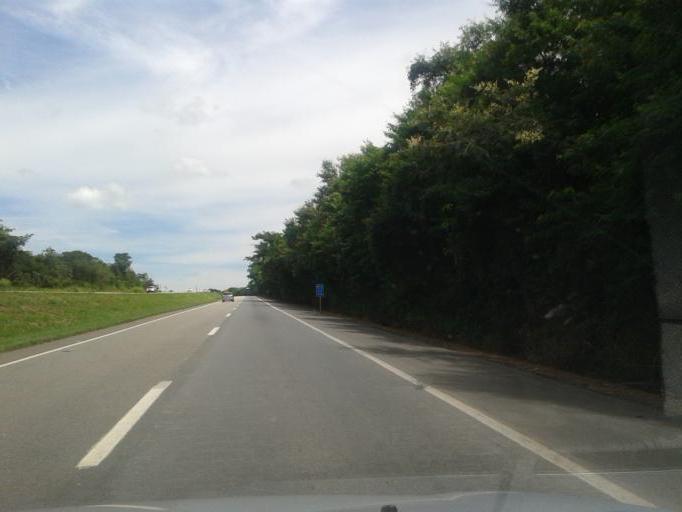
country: BR
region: Goias
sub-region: Hidrolandia
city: Hidrolandia
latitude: -17.0987
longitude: -49.2179
